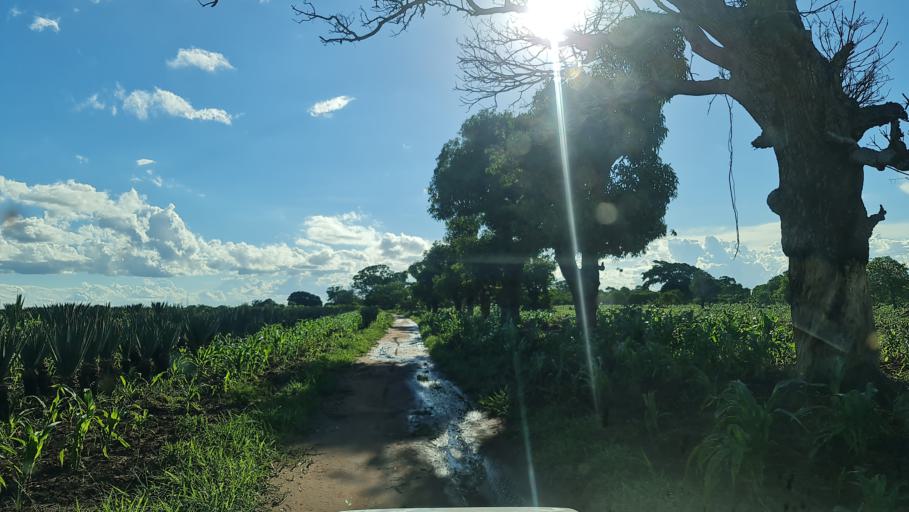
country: MZ
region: Nampula
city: Ilha de Mocambique
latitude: -14.9357
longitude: 40.2064
